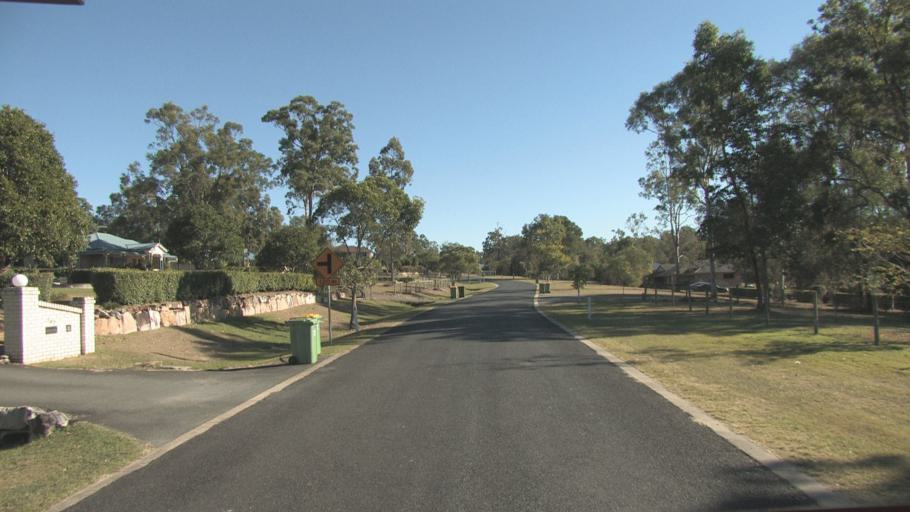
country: AU
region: Queensland
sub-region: Logan
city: North Maclean
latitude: -27.7434
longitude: 152.9648
